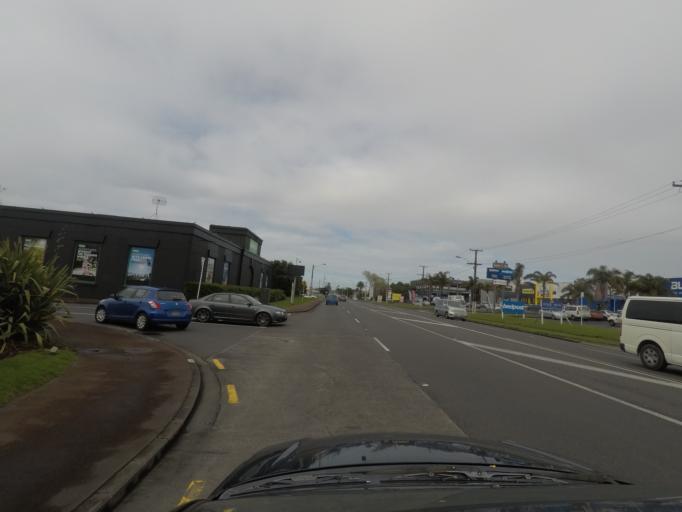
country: NZ
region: Auckland
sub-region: Auckland
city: Tamaki
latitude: -36.8994
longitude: 174.8444
